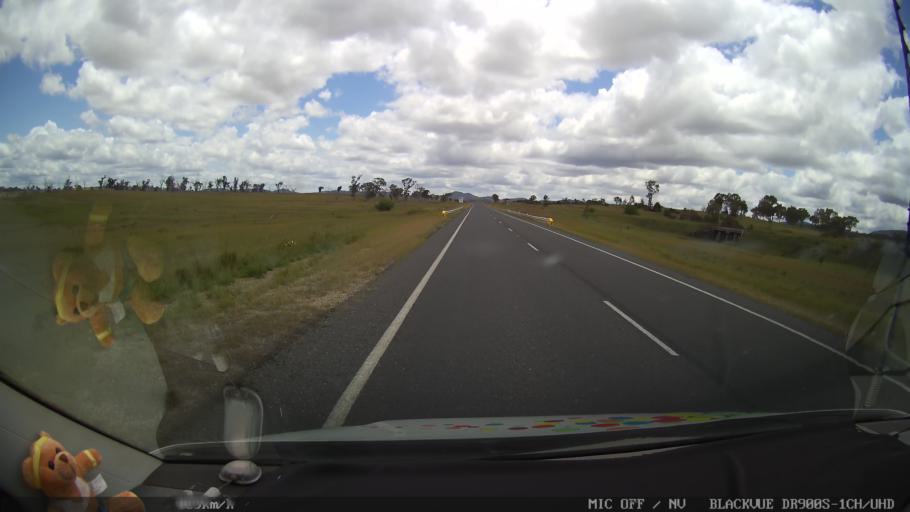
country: AU
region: New South Wales
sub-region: Glen Innes Severn
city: Glen Innes
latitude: -29.4087
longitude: 151.8690
